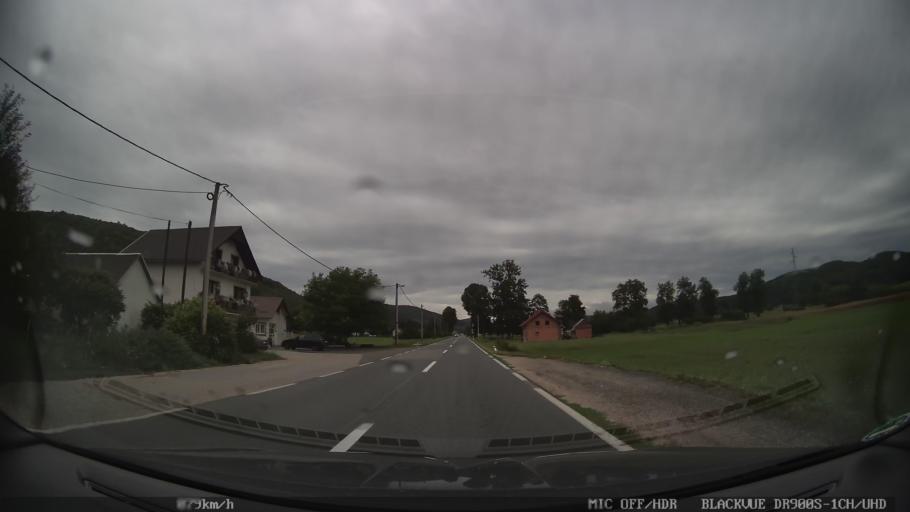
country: HR
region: Licko-Senjska
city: Brinje
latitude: 44.9169
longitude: 15.1547
